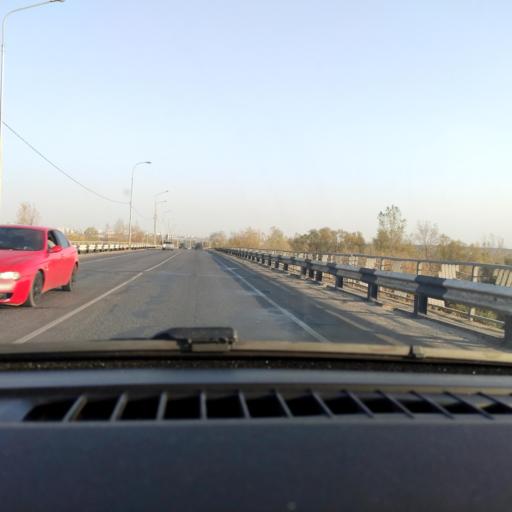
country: RU
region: Voronezj
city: Pridonskoy
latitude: 51.7235
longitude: 39.0624
